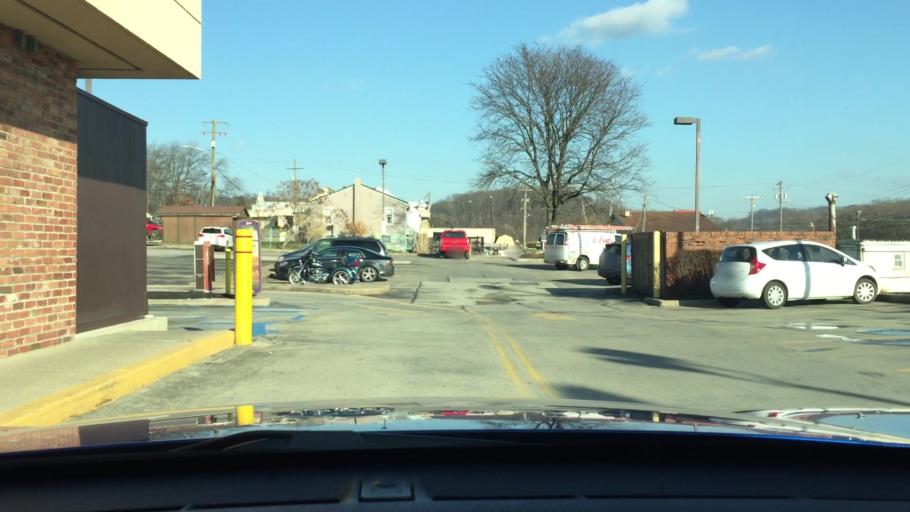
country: US
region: Pennsylvania
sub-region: Westmoreland County
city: New Stanton
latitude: 40.2192
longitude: -79.6094
